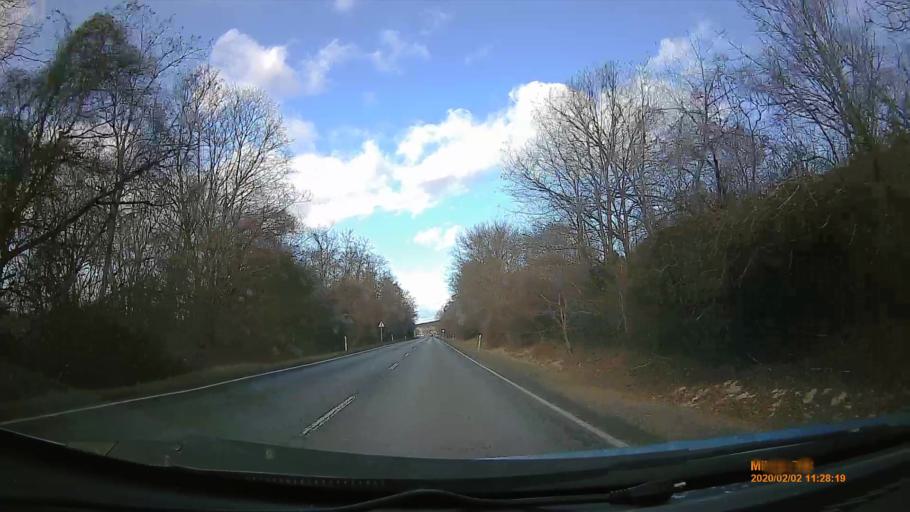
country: AT
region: Burgenland
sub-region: Eisenstadt-Umgebung
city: Klingenbach
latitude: 47.7263
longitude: 16.5598
